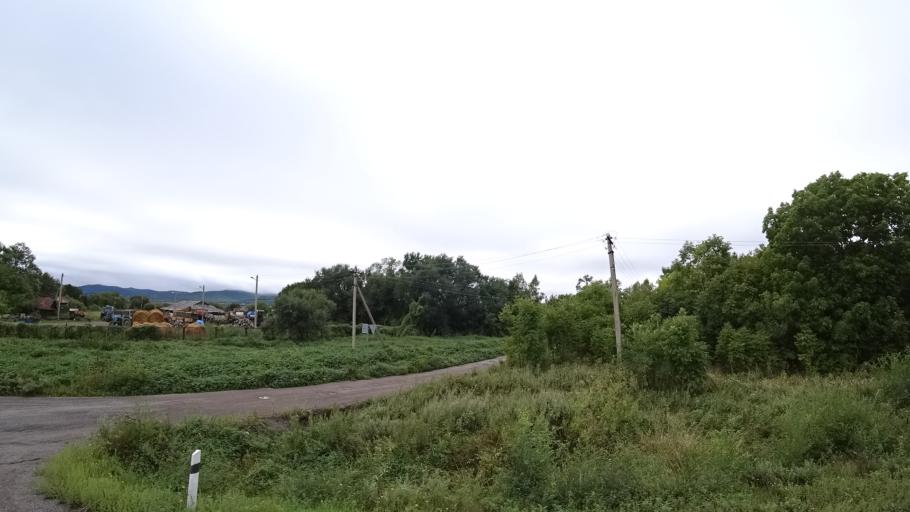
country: RU
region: Primorskiy
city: Monastyrishche
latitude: 44.1901
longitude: 132.4819
